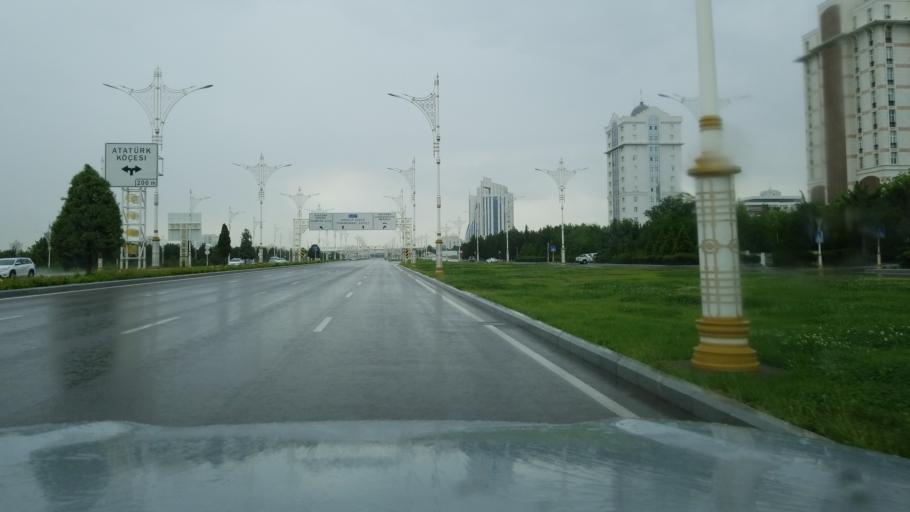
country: TM
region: Ahal
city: Ashgabat
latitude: 37.8858
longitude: 58.3556
